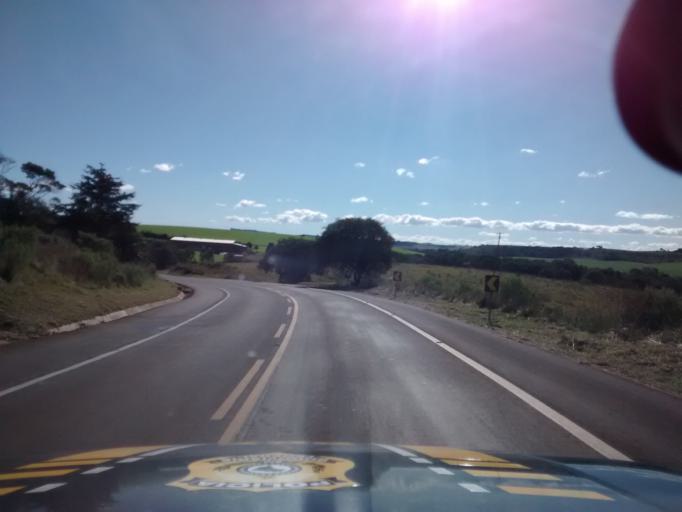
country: BR
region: Rio Grande do Sul
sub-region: Lagoa Vermelha
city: Lagoa Vermelha
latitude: -28.3342
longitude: -51.3115
